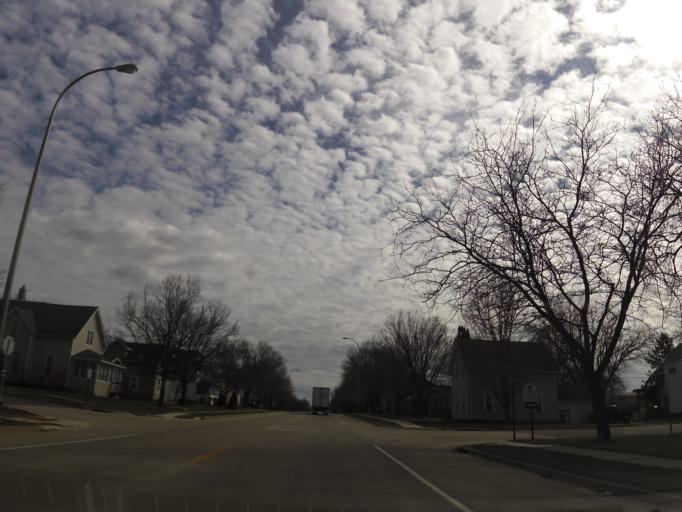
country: US
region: Minnesota
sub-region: Fillmore County
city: Spring Valley
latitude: 43.6835
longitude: -92.3893
